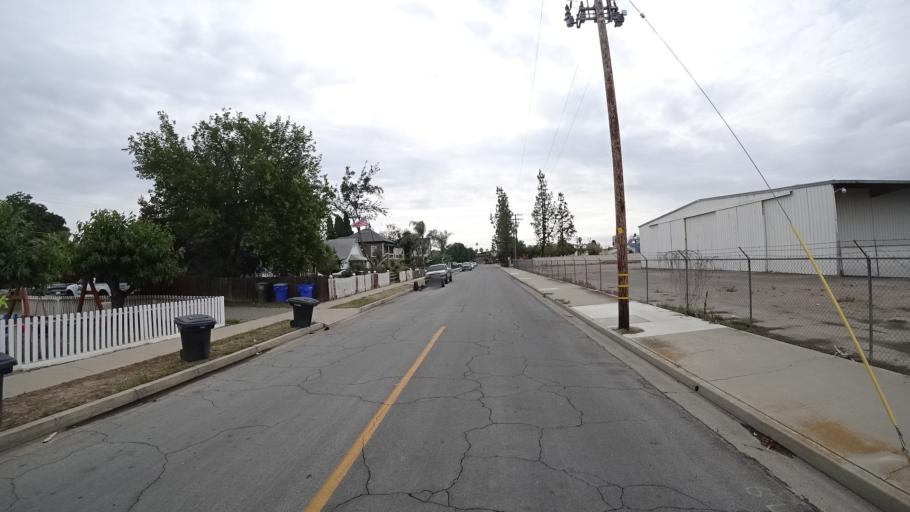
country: US
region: California
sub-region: Kings County
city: Hanford
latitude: 36.3289
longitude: -119.6527
